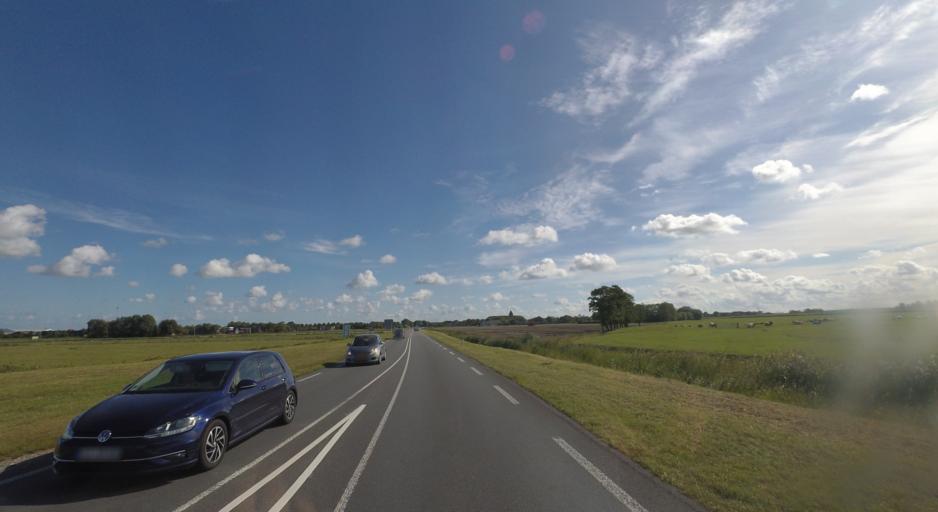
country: NL
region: Friesland
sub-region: Gemeente Leeuwarderadeel
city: Stiens
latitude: 53.2638
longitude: 5.7395
